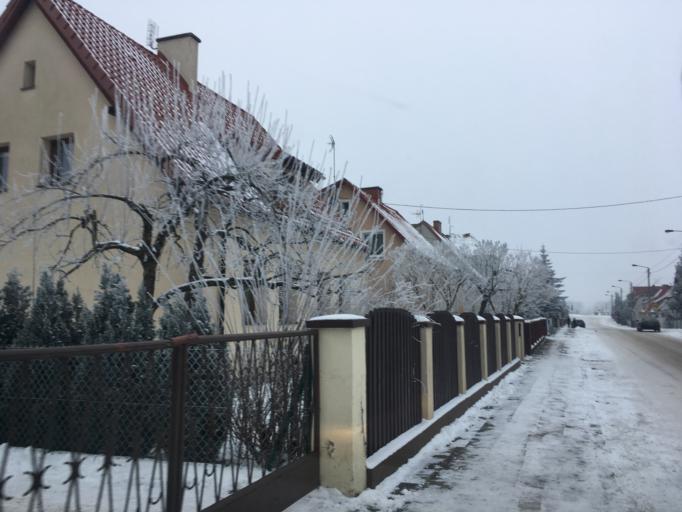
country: PL
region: Warmian-Masurian Voivodeship
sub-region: Powiat olsztynski
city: Biskupiec
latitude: 53.8679
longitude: 20.9600
